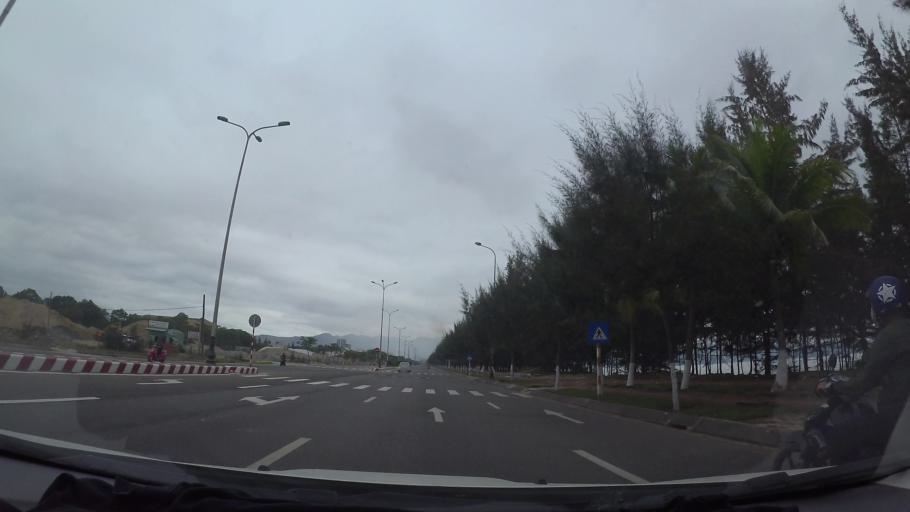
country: VN
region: Da Nang
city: Lien Chieu
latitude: 16.1019
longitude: 108.1395
